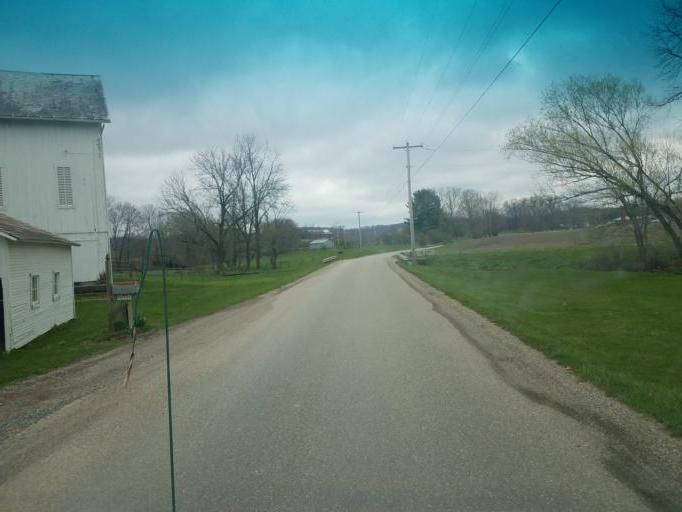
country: US
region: Ohio
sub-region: Stark County
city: Beach City
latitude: 40.6357
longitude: -81.5865
